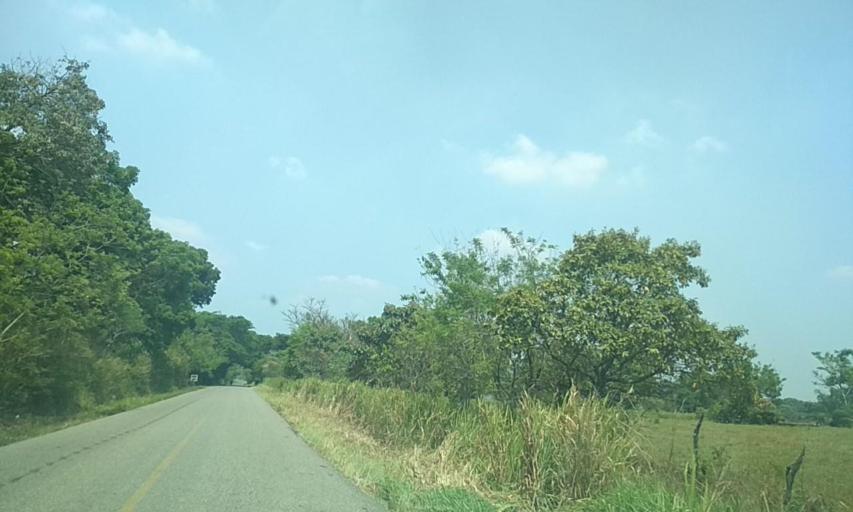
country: MX
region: Tabasco
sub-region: Cardenas
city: Poblado C-33 20 de Noviembre
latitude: 17.8419
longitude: -93.5543
